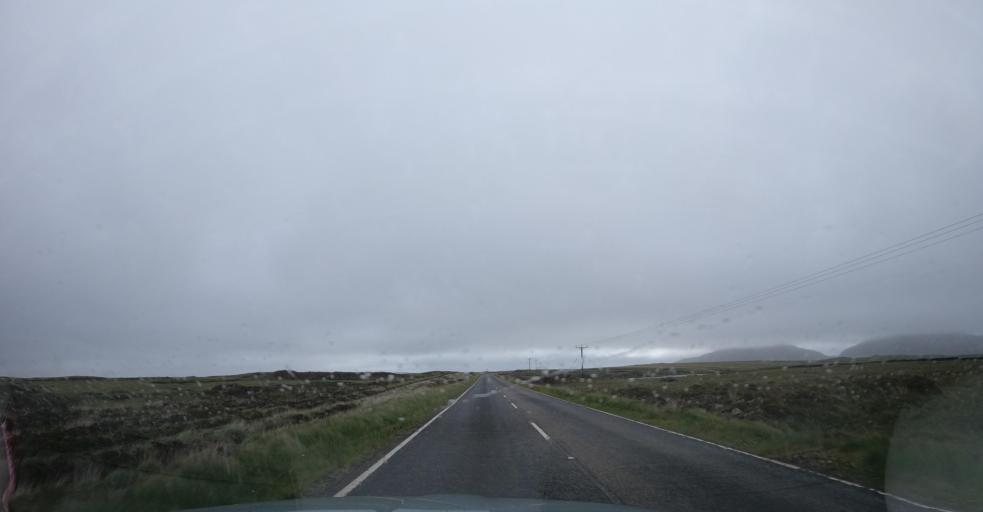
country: GB
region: Scotland
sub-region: Eilean Siar
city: Isle of North Uist
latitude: 57.5931
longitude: -7.2115
